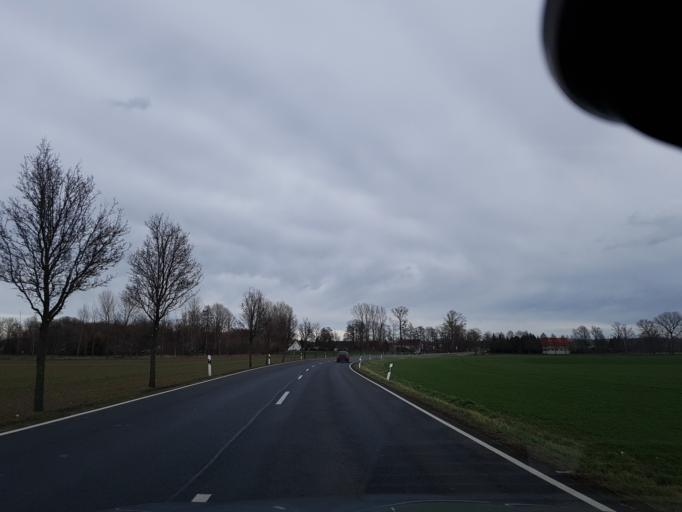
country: DE
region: Saxony
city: Stauchitz
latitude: 51.2361
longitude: 13.1821
